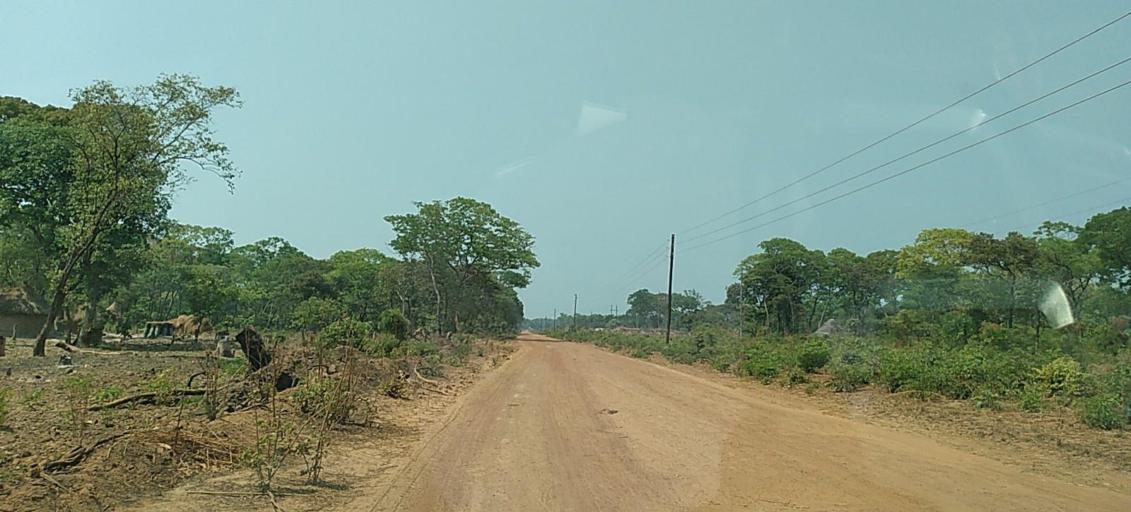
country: ZM
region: Copperbelt
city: Kalulushi
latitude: -13.0972
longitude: 27.4055
